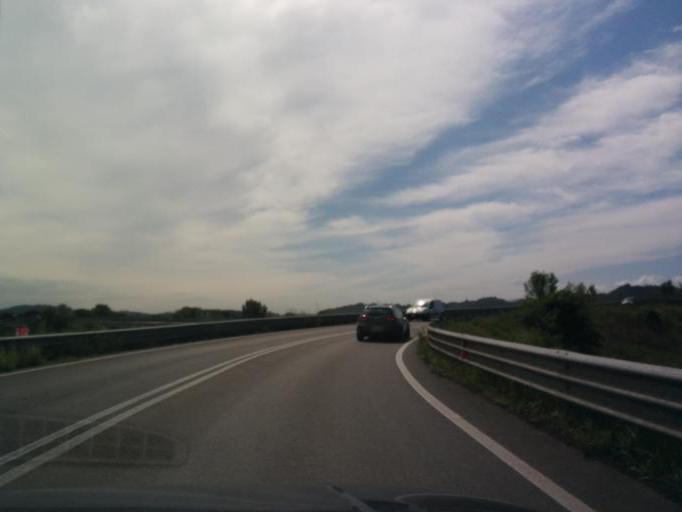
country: IT
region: Tuscany
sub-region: Provincia di Siena
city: Poggibonsi
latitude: 43.4835
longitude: 11.1262
